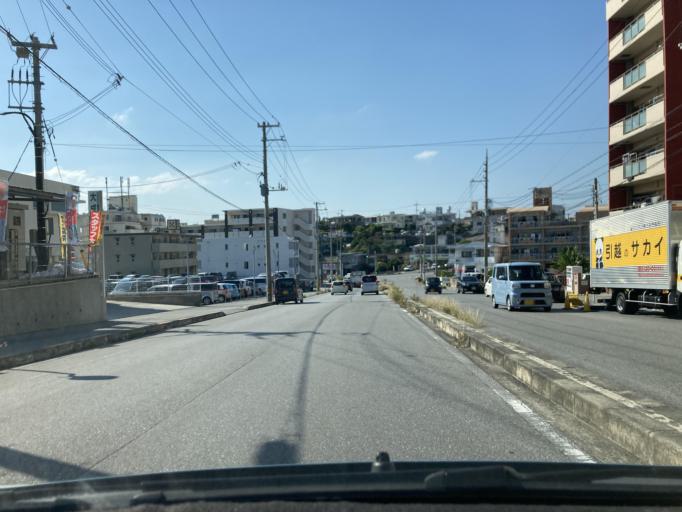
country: JP
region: Okinawa
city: Ginowan
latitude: 26.2363
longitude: 127.7223
